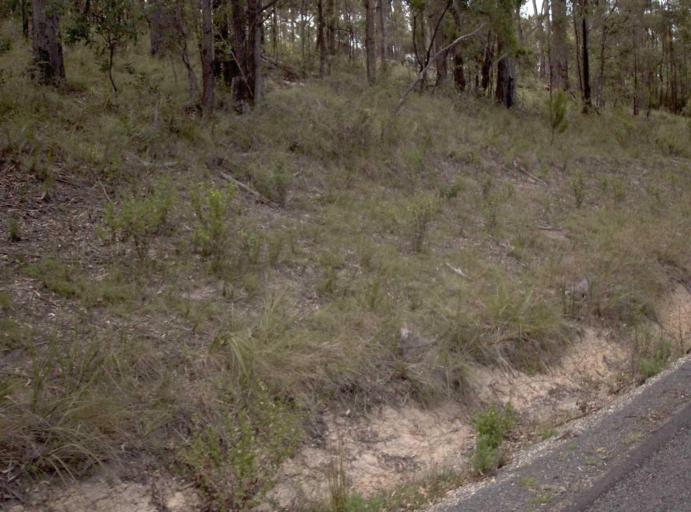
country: AU
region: New South Wales
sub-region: Bega Valley
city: Eden
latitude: -37.3839
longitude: 149.6851
